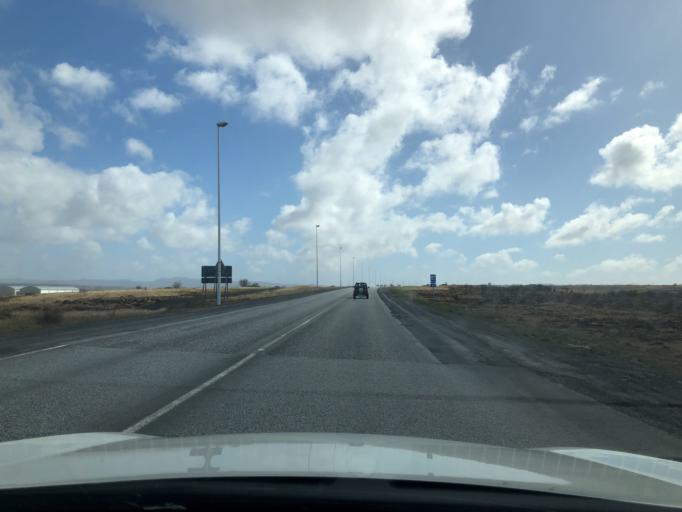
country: IS
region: Southern Peninsula
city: Reykjanesbaer
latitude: 63.9962
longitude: -22.5874
